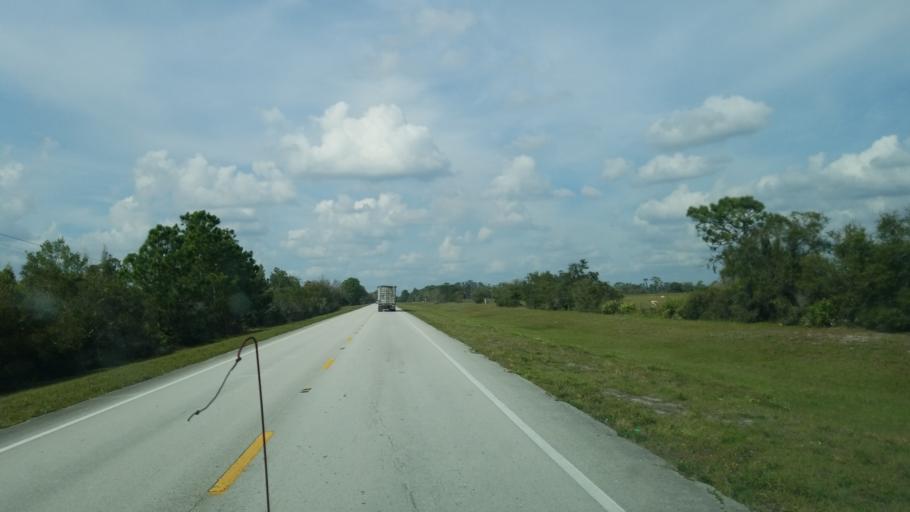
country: US
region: Florida
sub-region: Indian River County
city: Fellsmere
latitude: 27.7118
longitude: -80.9105
